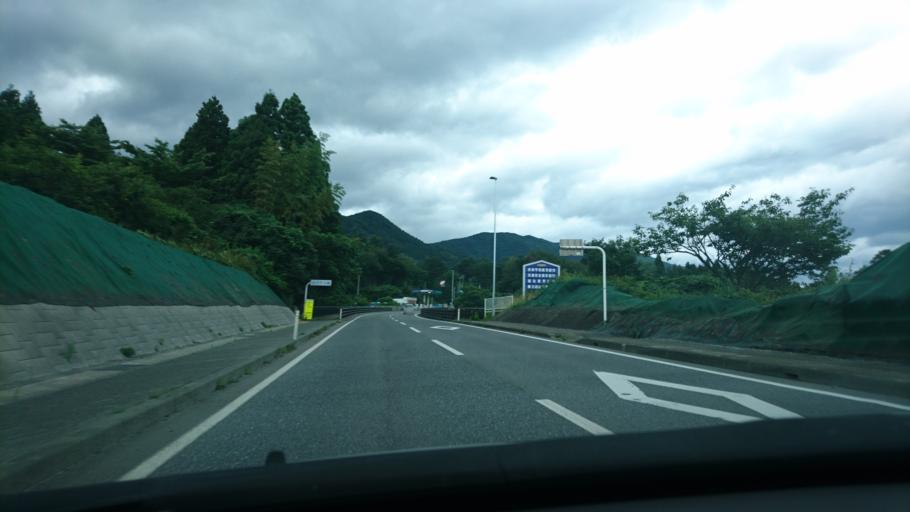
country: JP
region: Iwate
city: Kamaishi
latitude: 39.1534
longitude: 141.8370
